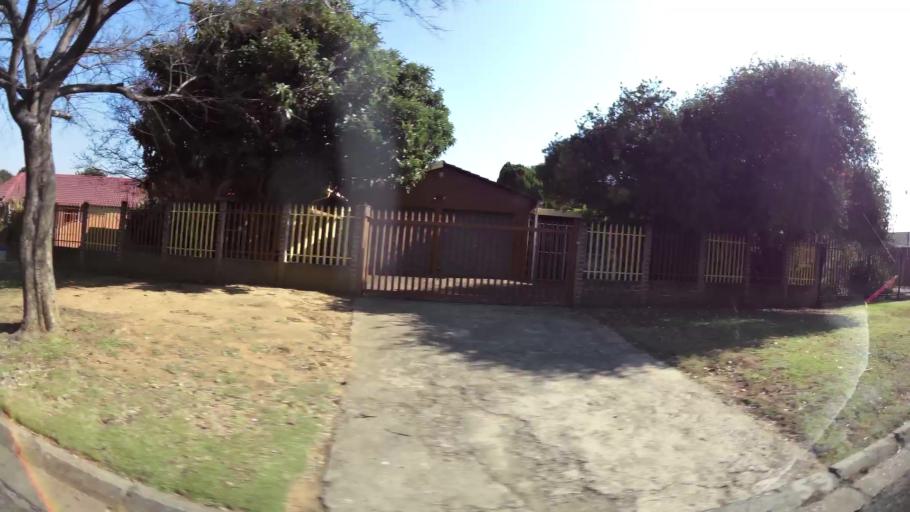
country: ZA
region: Gauteng
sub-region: Ekurhuleni Metropolitan Municipality
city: Boksburg
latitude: -26.1585
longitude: 28.2580
